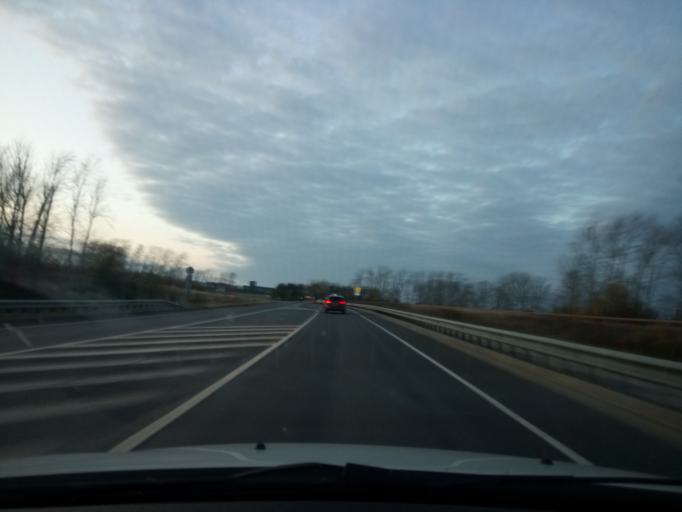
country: RU
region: Nizjnij Novgorod
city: Bol'shoye Murashkino
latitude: 55.8852
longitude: 44.7471
